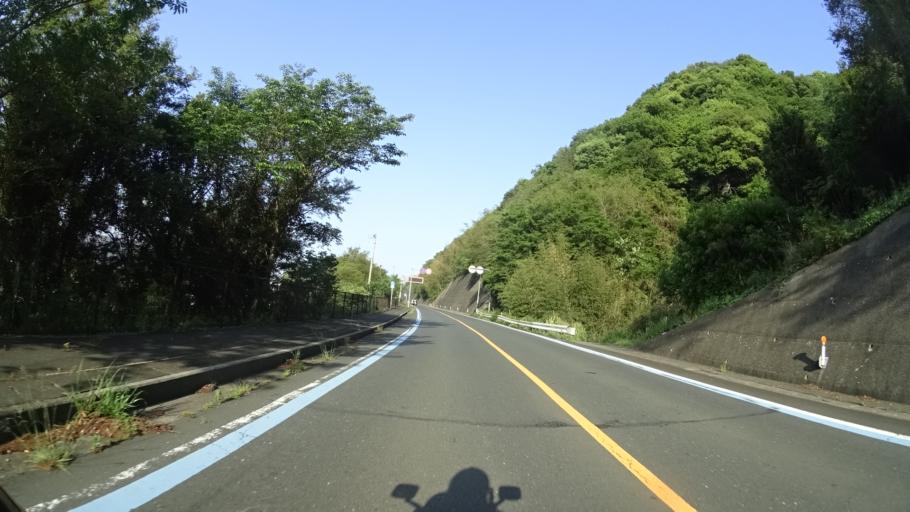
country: JP
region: Ehime
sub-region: Nishiuwa-gun
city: Ikata-cho
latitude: 33.4928
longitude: 132.3583
